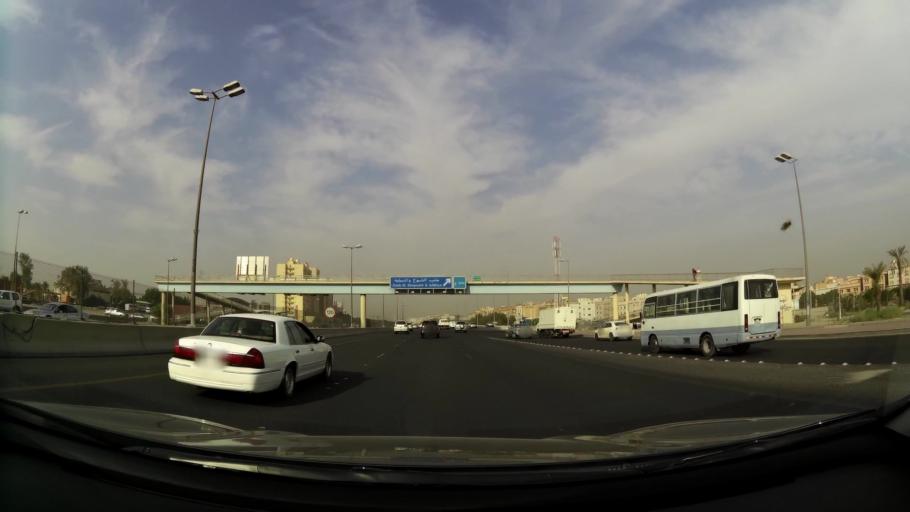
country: KW
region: Al Farwaniyah
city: Al Farwaniyah
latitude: 29.2665
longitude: 47.9471
